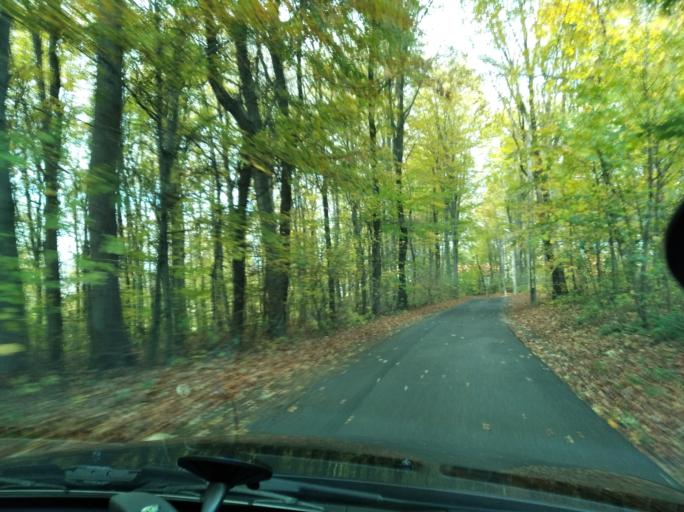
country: PL
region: Subcarpathian Voivodeship
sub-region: Powiat debicki
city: Debica
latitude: 50.0325
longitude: 21.4539
